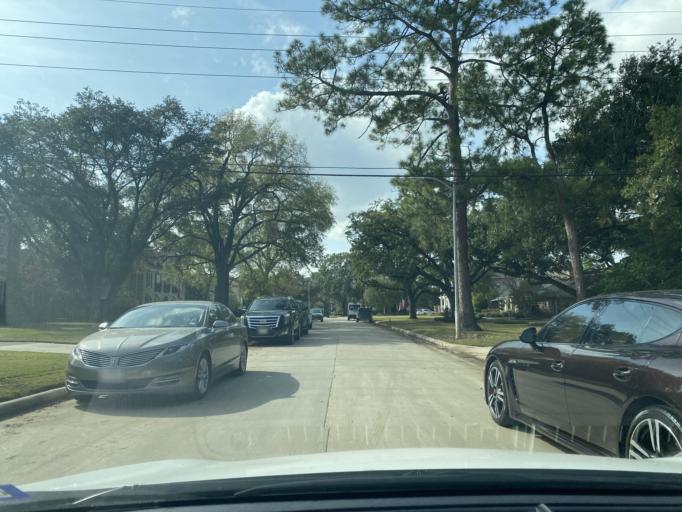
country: US
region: Texas
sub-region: Harris County
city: Hunters Creek Village
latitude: 29.7599
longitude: -95.4713
